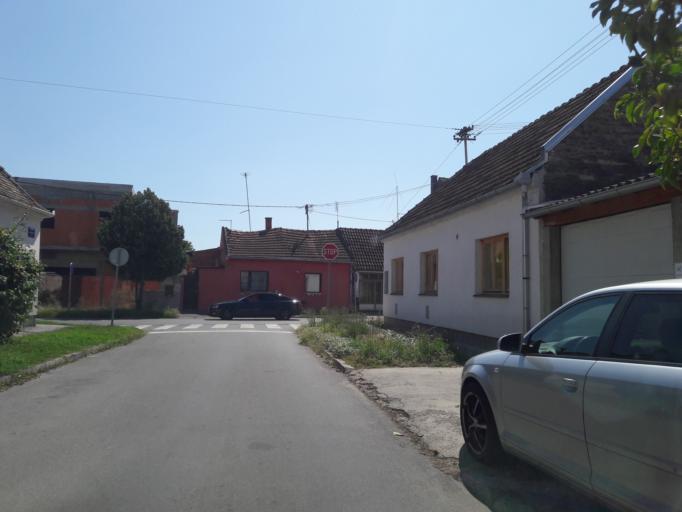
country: HR
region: Osjecko-Baranjska
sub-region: Grad Osijek
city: Osijek
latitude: 45.5598
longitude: 18.6595
